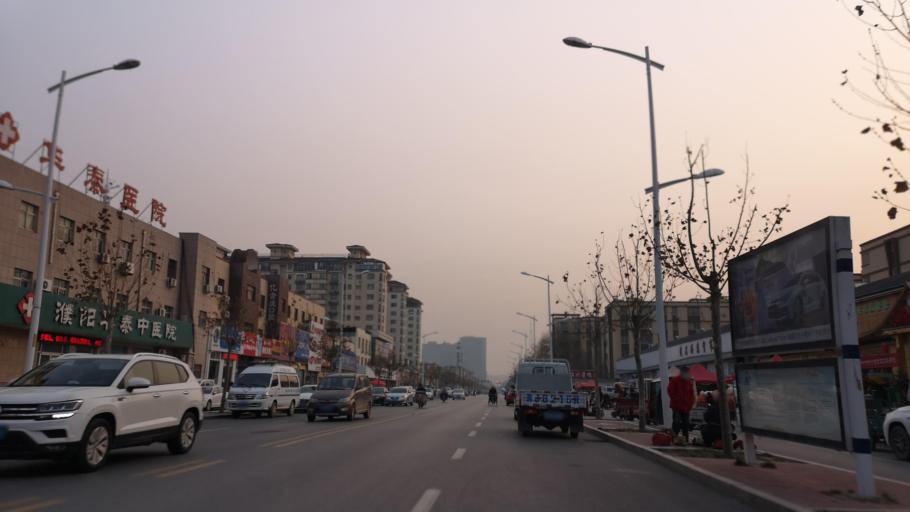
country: CN
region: Henan Sheng
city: Zhongyuanlu
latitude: 35.7869
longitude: 115.0817
